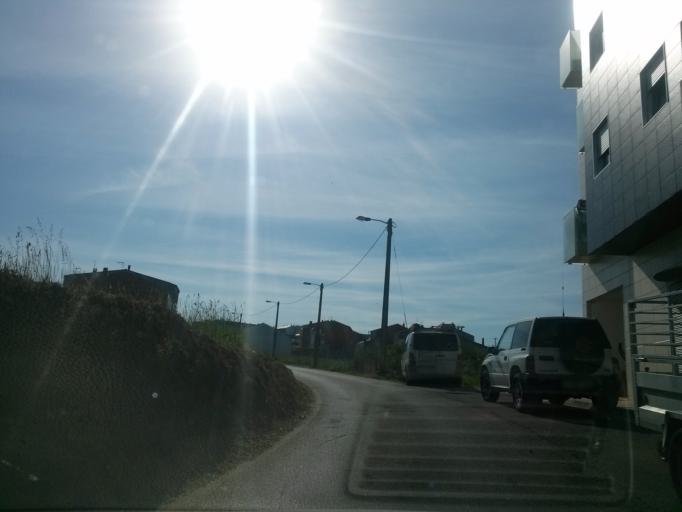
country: ES
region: Galicia
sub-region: Provincia de Lugo
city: Lugo
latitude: 43.0296
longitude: -7.5636
